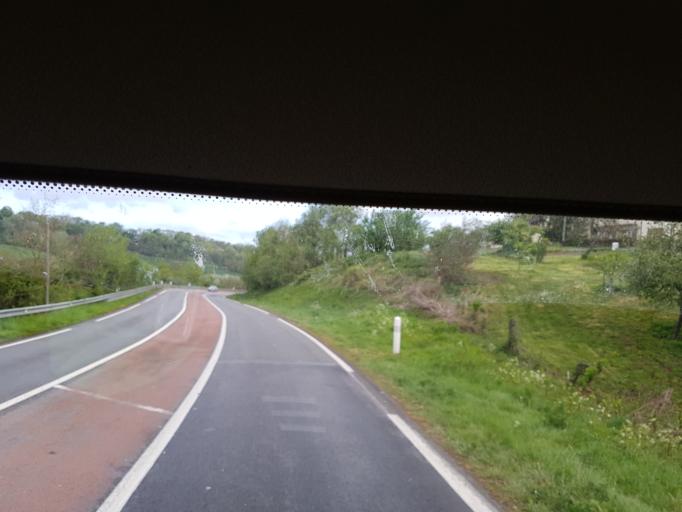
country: FR
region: Picardie
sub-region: Departement de l'Aisne
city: Coucy-le-Chateau-Auffrique
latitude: 49.4772
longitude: 3.3436
